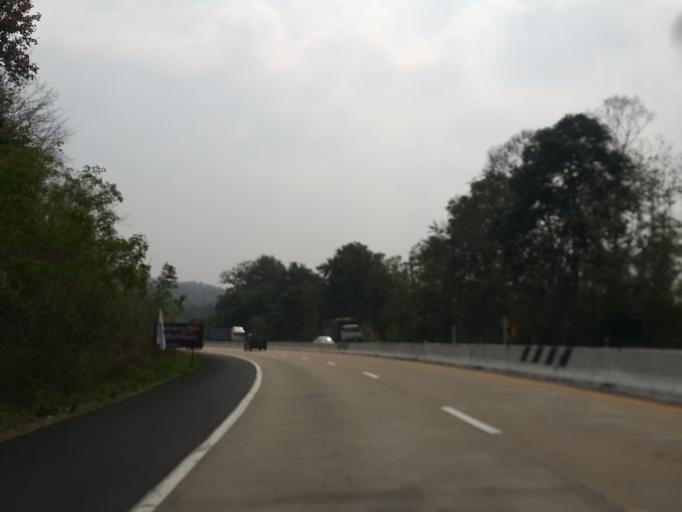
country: TH
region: Lampang
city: Hang Chat
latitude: 18.3605
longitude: 99.2384
